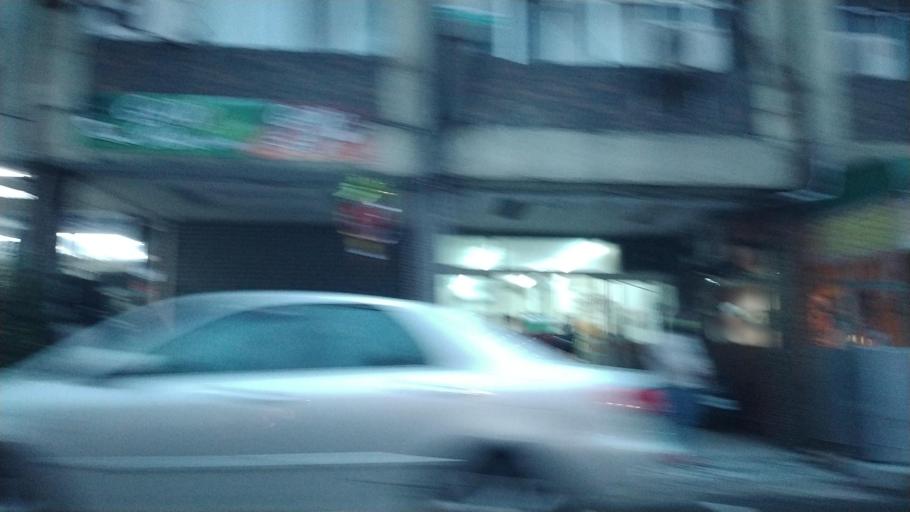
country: TW
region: Taiwan
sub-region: Hualien
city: Hualian
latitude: 23.9768
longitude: 121.6013
